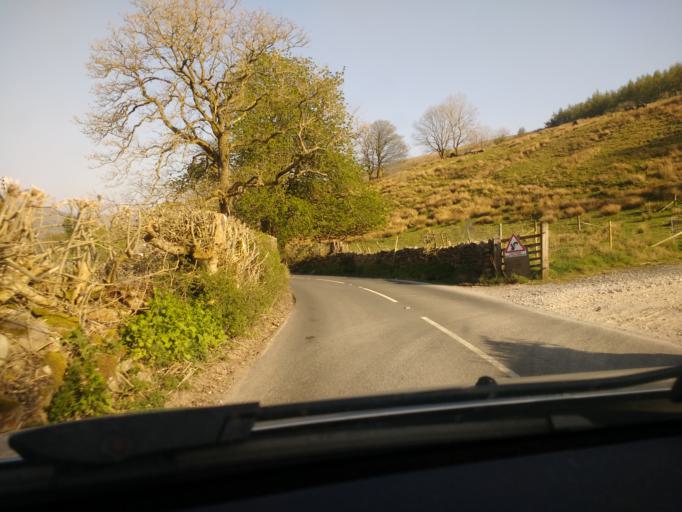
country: GB
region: England
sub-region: Cumbria
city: Sedbergh
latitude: 54.3129
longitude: -2.4588
